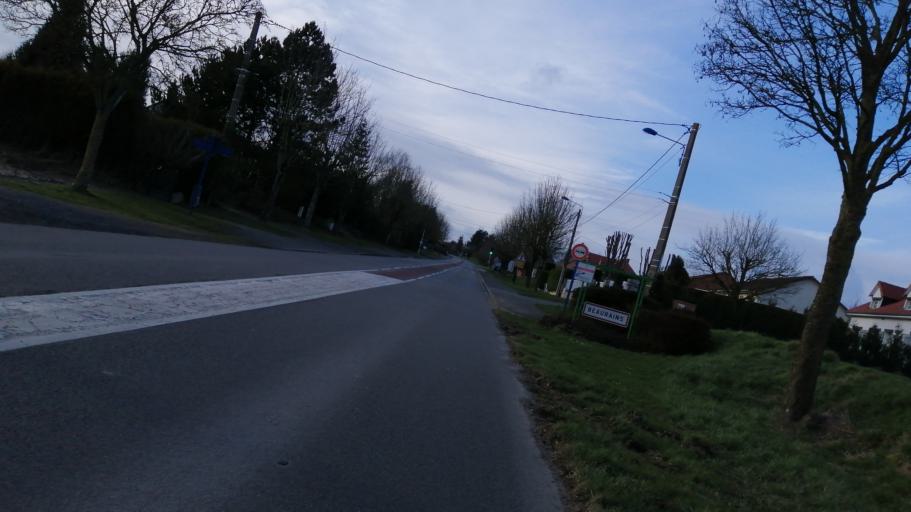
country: FR
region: Nord-Pas-de-Calais
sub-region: Departement du Pas-de-Calais
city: Beaurains
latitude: 50.2557
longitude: 2.8044
